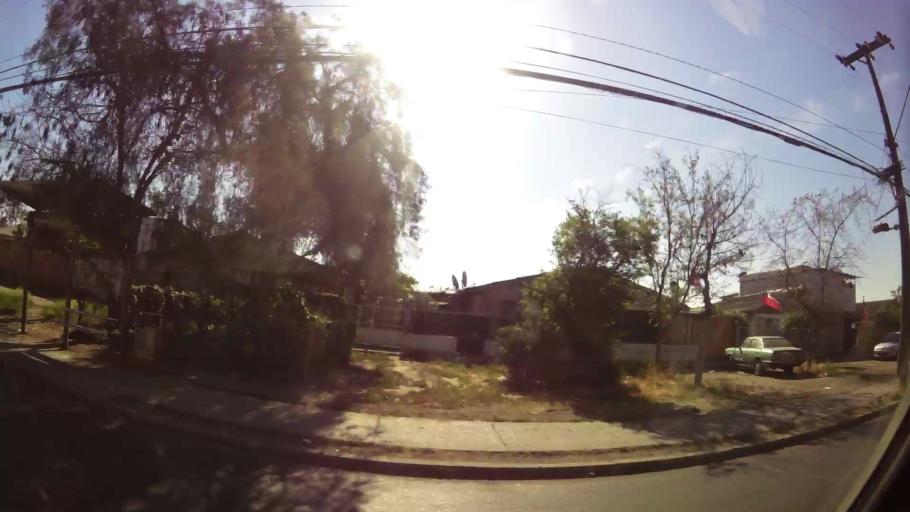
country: CL
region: Santiago Metropolitan
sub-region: Provincia de Santiago
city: Santiago
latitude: -33.5078
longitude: -70.6783
